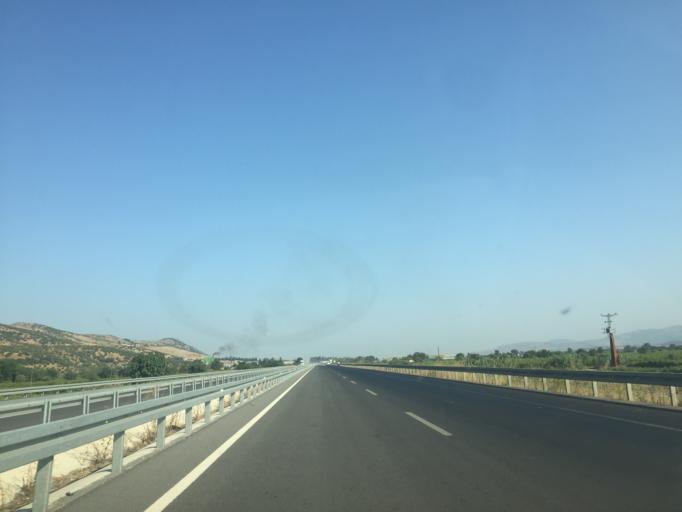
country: TR
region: Manisa
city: Golmarmara
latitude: 38.6856
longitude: 27.9398
